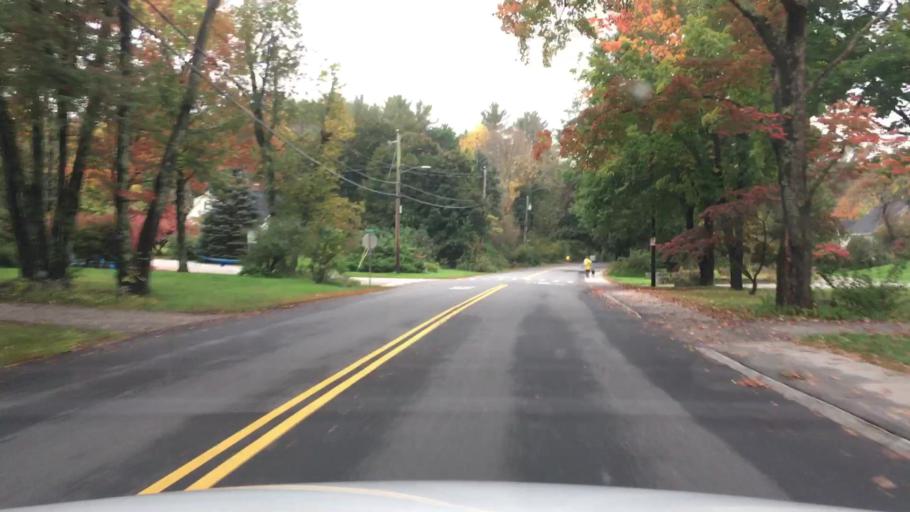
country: US
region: New Hampshire
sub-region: Strafford County
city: Durham
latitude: 43.1434
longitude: -70.9284
